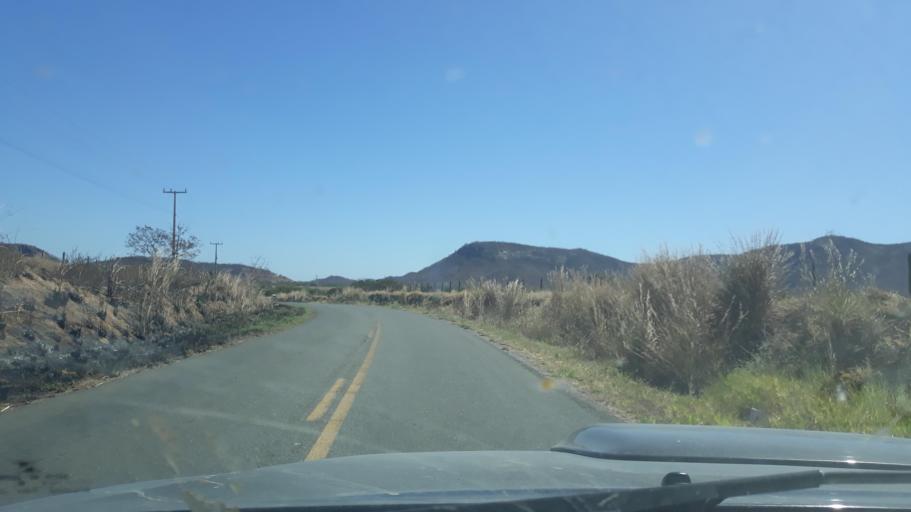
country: BR
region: Bahia
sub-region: Guanambi
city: Guanambi
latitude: -14.1546
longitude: -42.8216
